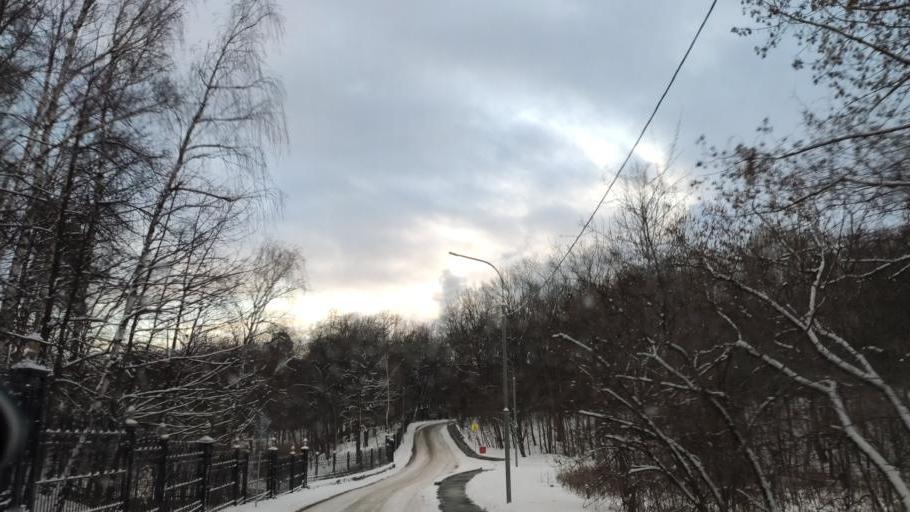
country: RU
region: Moscow
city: Orekhovo-Borisovo Severnoye
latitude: 55.6101
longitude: 37.6734
